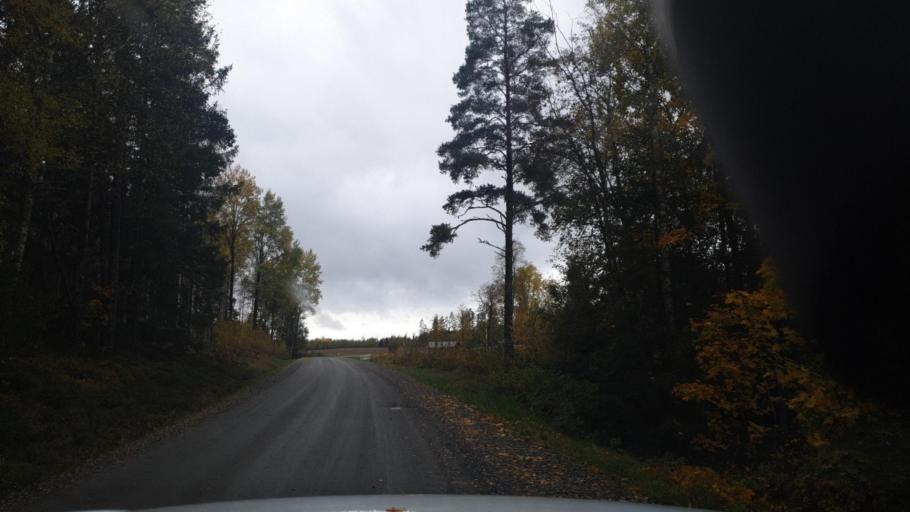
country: SE
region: Vaermland
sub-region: Karlstads Kommun
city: Edsvalla
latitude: 59.4493
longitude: 13.1229
